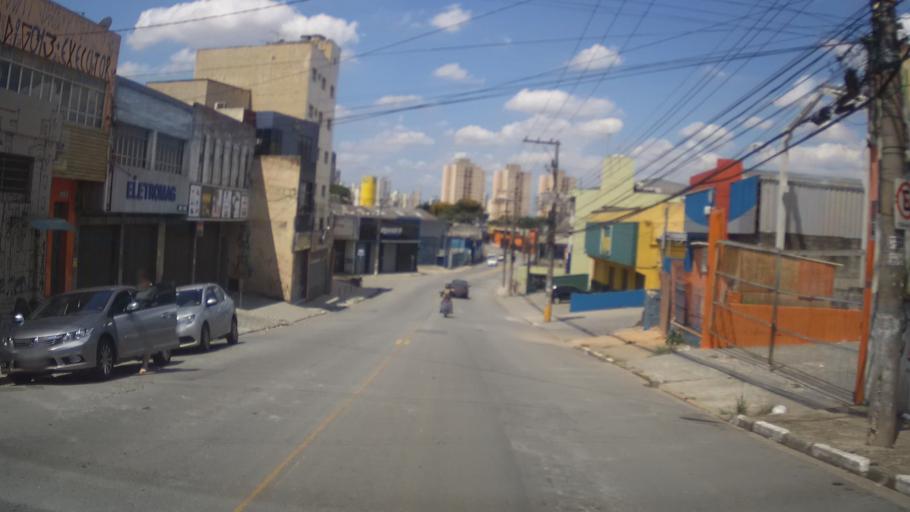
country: BR
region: Sao Paulo
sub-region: Guarulhos
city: Guarulhos
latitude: -23.4797
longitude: -46.5389
